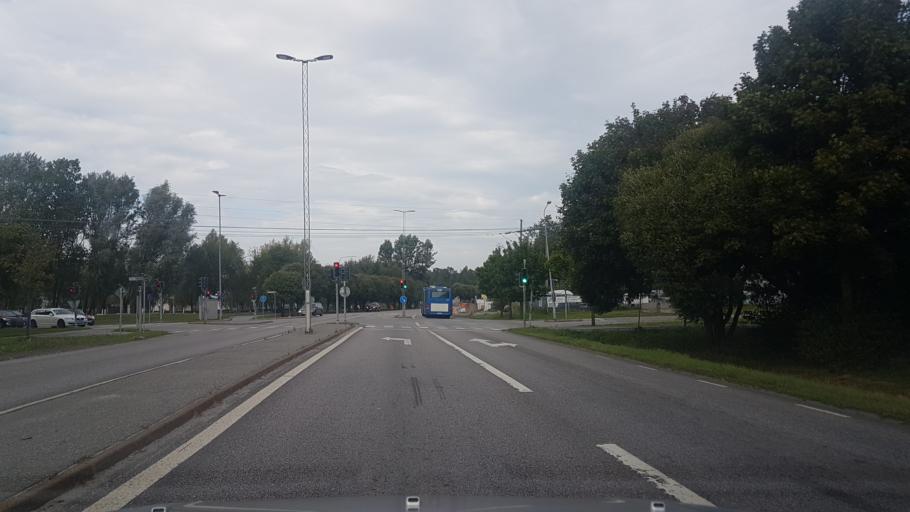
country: SE
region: Stockholm
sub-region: Jarfalla Kommun
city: Jakobsberg
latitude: 59.4143
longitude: 17.8287
